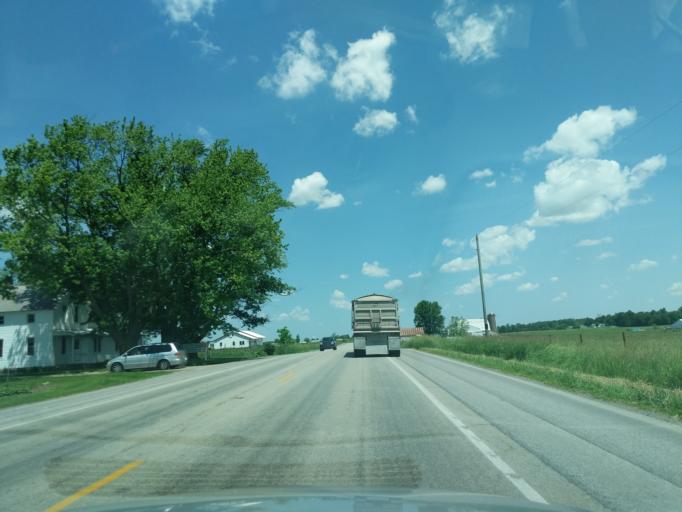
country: US
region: Indiana
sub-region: LaGrange County
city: Topeka
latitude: 41.6365
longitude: -85.5799
